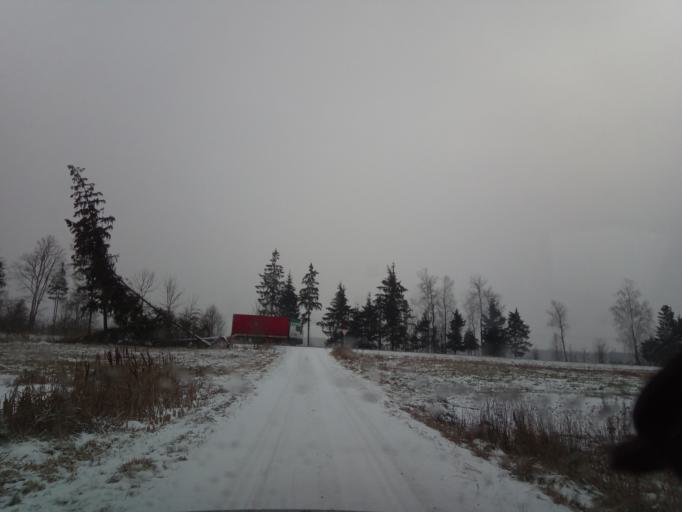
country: LT
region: Utenos apskritis
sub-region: Anyksciai
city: Anyksciai
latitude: 55.4020
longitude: 25.1699
